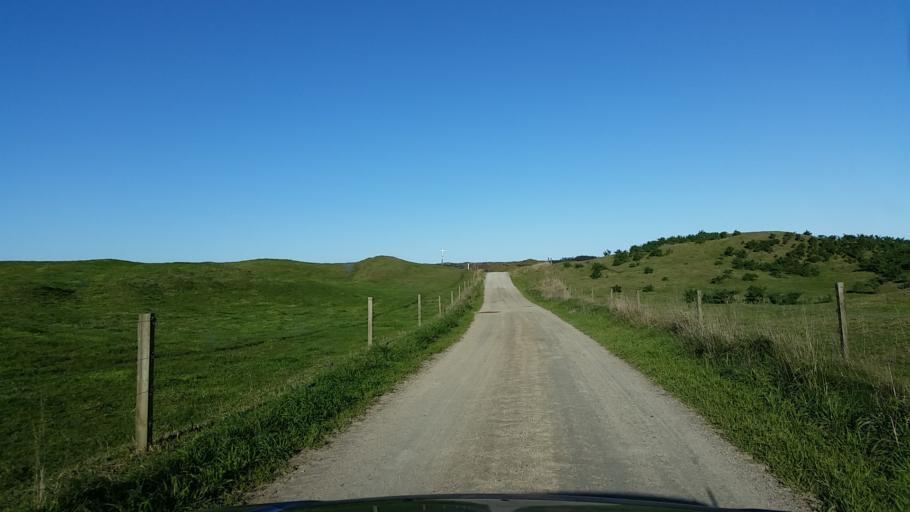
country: NZ
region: Taranaki
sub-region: South Taranaki District
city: Patea
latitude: -39.8356
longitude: 174.6855
